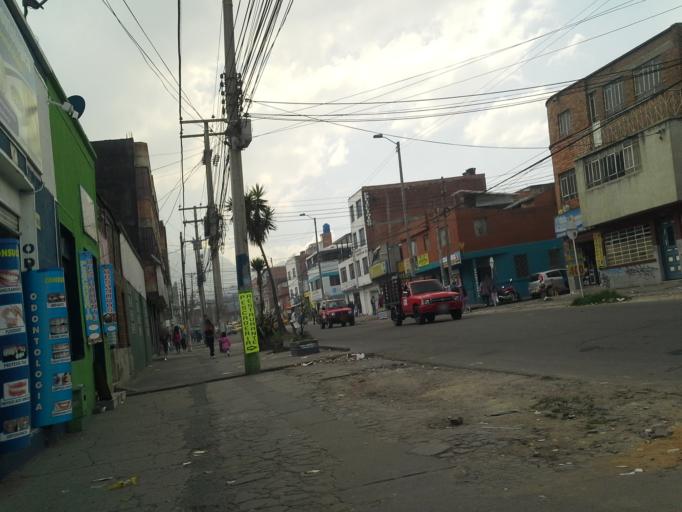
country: CO
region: Bogota D.C.
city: Bogota
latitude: 4.5810
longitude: -74.1078
